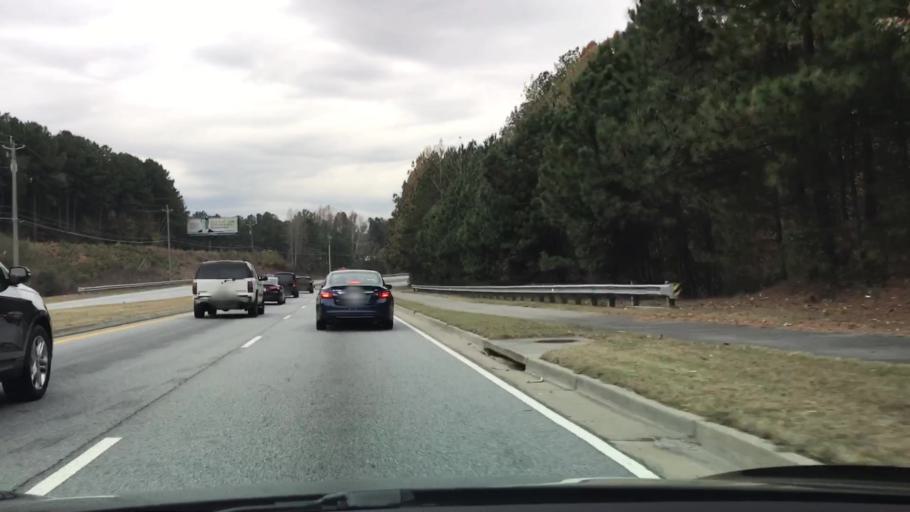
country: US
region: Georgia
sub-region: Gwinnett County
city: Berkeley Lake
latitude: 33.9804
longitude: -84.1725
